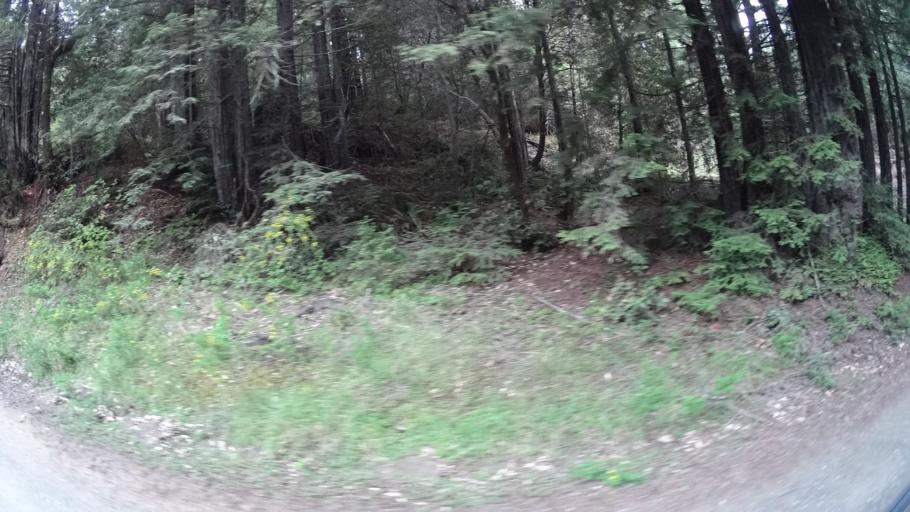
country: US
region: California
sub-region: Humboldt County
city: Redway
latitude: 40.3161
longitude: -123.8302
